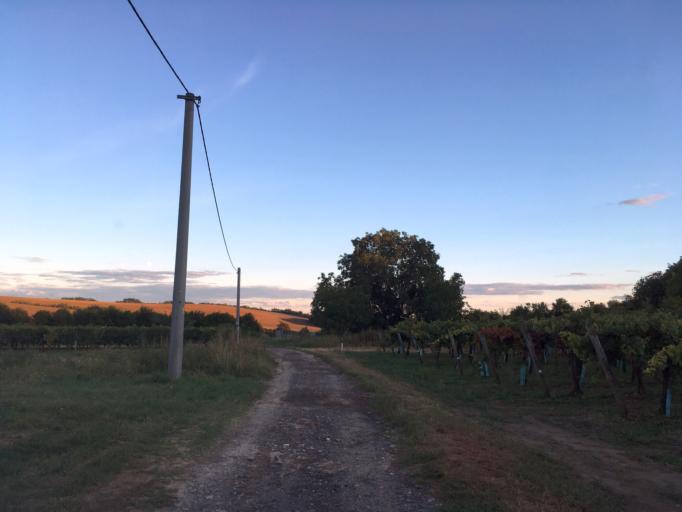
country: SK
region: Nitriansky
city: Svodin
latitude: 47.9121
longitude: 18.4403
